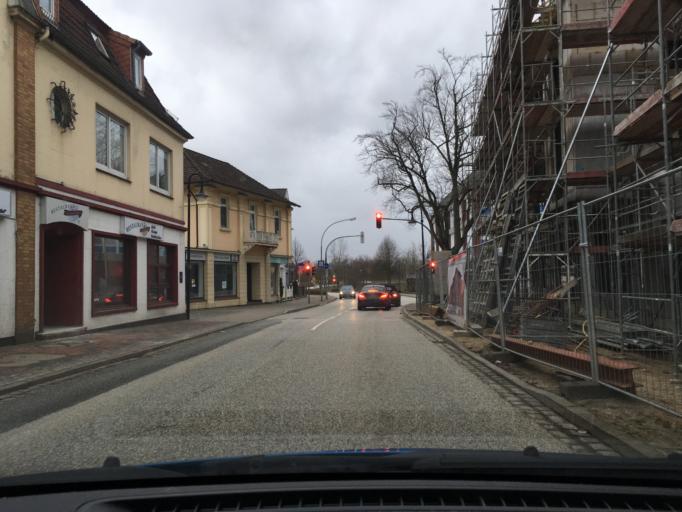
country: DE
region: Schleswig-Holstein
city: Schwarzenbek
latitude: 53.5023
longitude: 10.4791
